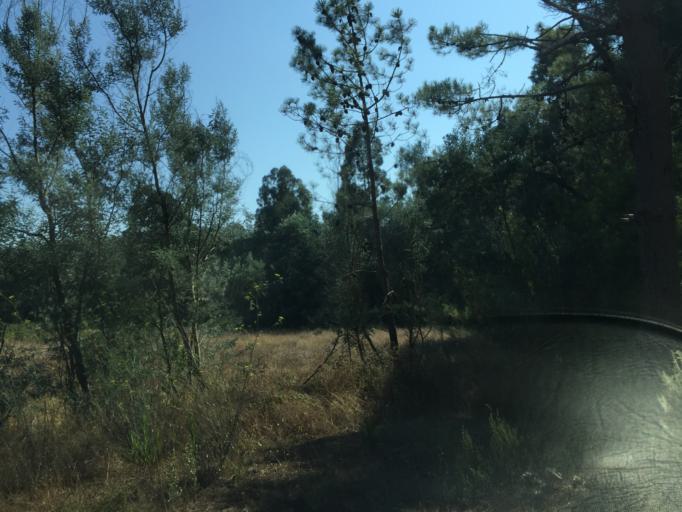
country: PT
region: Coimbra
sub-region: Figueira da Foz
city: Tavarede
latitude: 40.2284
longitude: -8.8533
